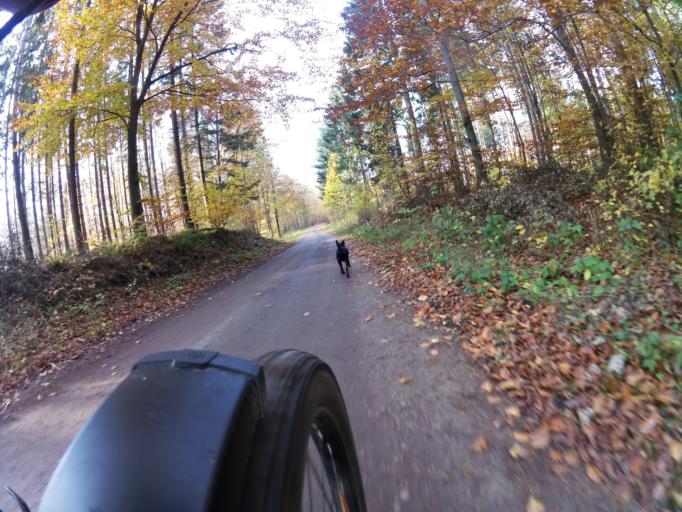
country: PL
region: Pomeranian Voivodeship
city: Strzelno
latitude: 54.7402
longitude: 18.2580
